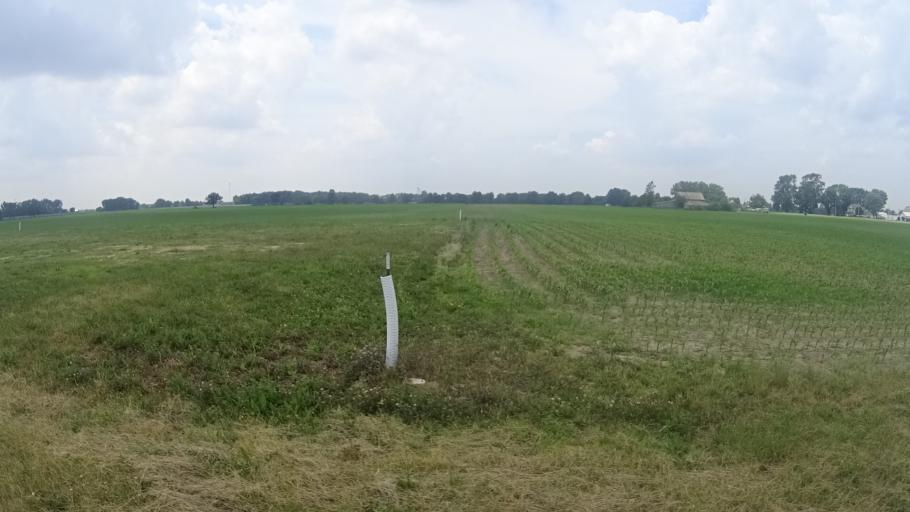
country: US
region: Ohio
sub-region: Erie County
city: Milan
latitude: 41.3213
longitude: -82.6735
